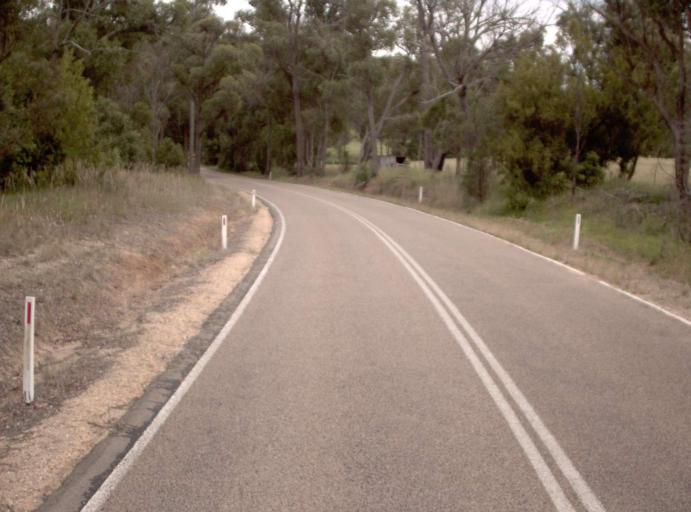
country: AU
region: Victoria
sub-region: East Gippsland
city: Bairnsdale
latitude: -37.7763
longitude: 147.5983
